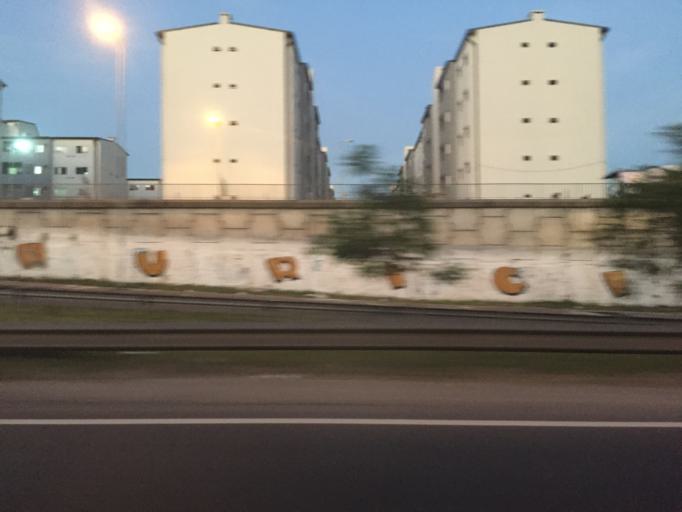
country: AR
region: Buenos Aires F.D.
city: Villa Lugano
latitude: -34.6833
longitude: -58.4899
